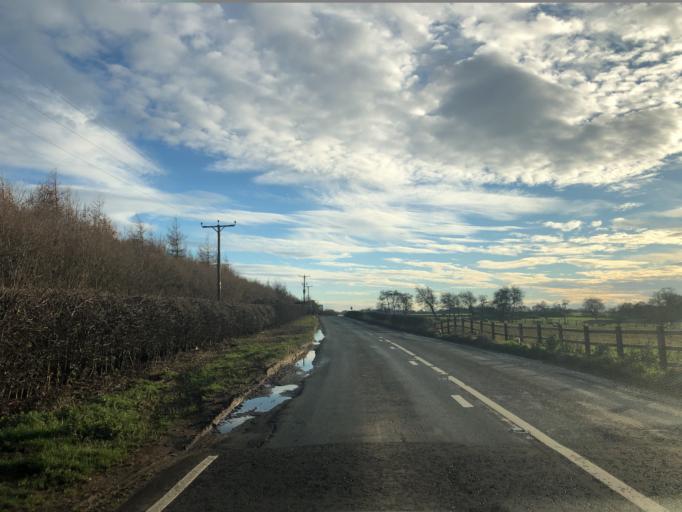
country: GB
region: England
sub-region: North Yorkshire
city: Thirsk
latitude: 54.1779
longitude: -1.3701
